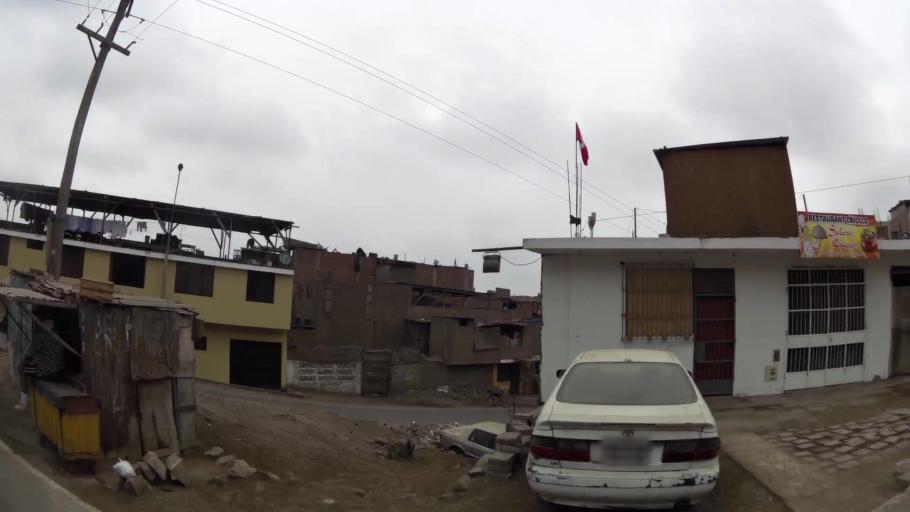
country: PE
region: Lima
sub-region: Lima
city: Surco
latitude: -12.1381
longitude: -76.9579
